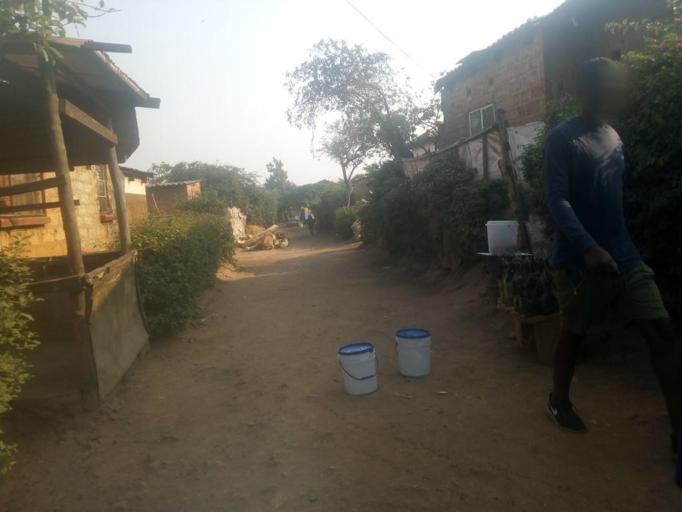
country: ZM
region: Lusaka
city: Lusaka
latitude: -15.4085
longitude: 28.3648
